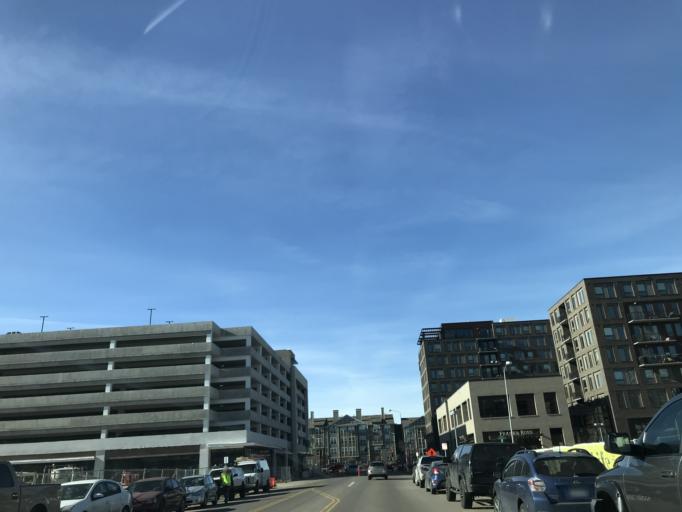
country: US
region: Colorado
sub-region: Arapahoe County
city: Glendale
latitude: 39.7311
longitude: -104.9387
